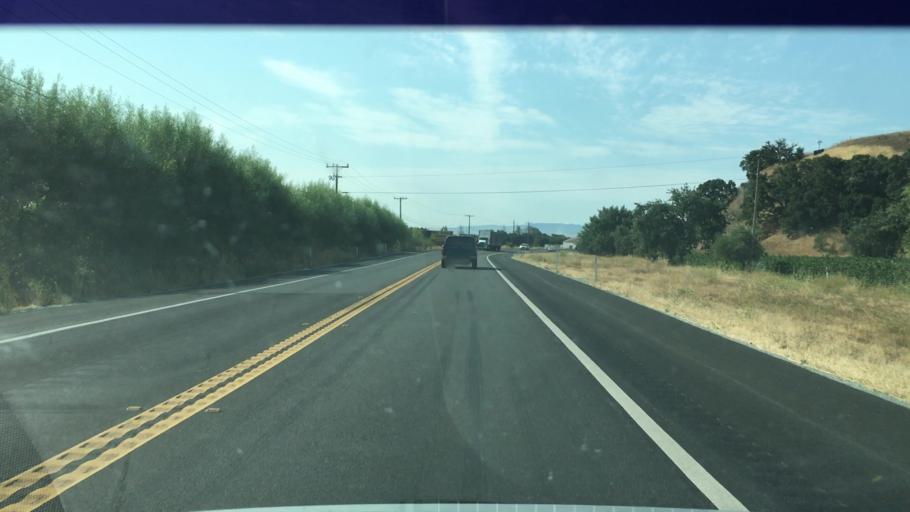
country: US
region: California
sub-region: San Benito County
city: Hollister
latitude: 36.9549
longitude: -121.3830
